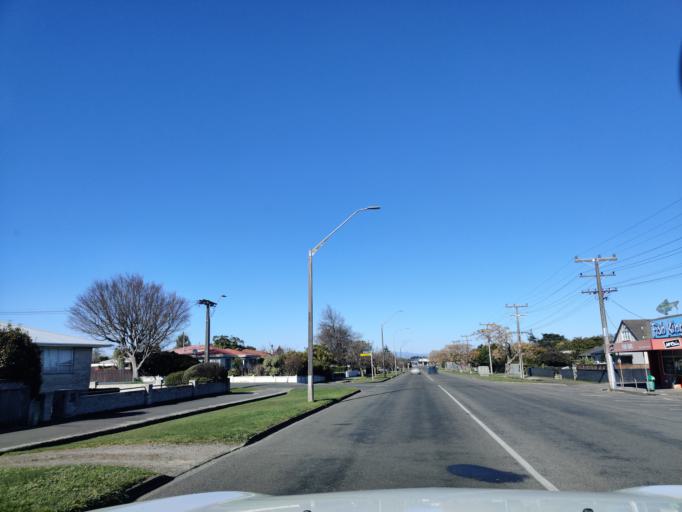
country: NZ
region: Manawatu-Wanganui
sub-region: Palmerston North City
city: Palmerston North
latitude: -40.2291
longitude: 175.5750
